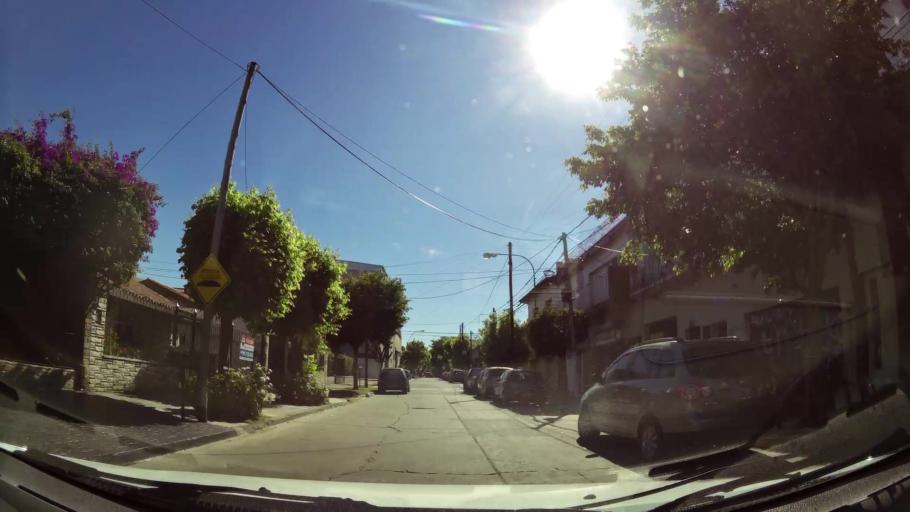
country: AR
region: Buenos Aires
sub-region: Partido de General San Martin
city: General San Martin
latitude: -34.5474
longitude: -58.5184
